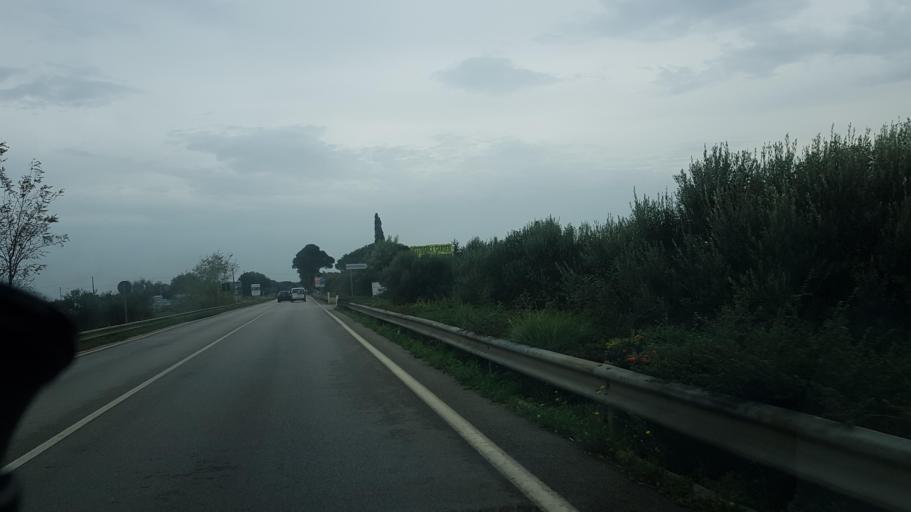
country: IT
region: Apulia
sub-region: Provincia di Brindisi
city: Carovigno
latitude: 40.7158
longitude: 17.6206
